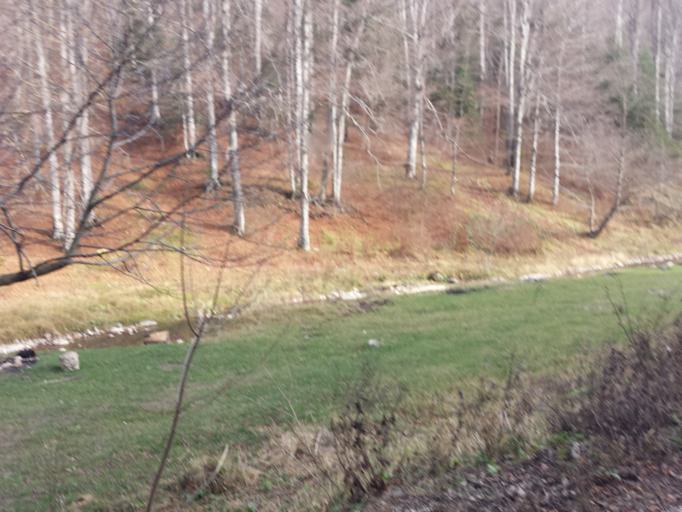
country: RO
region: Prahova
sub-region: Oras Azuga
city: Azuga
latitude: 45.4280
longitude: 25.5367
